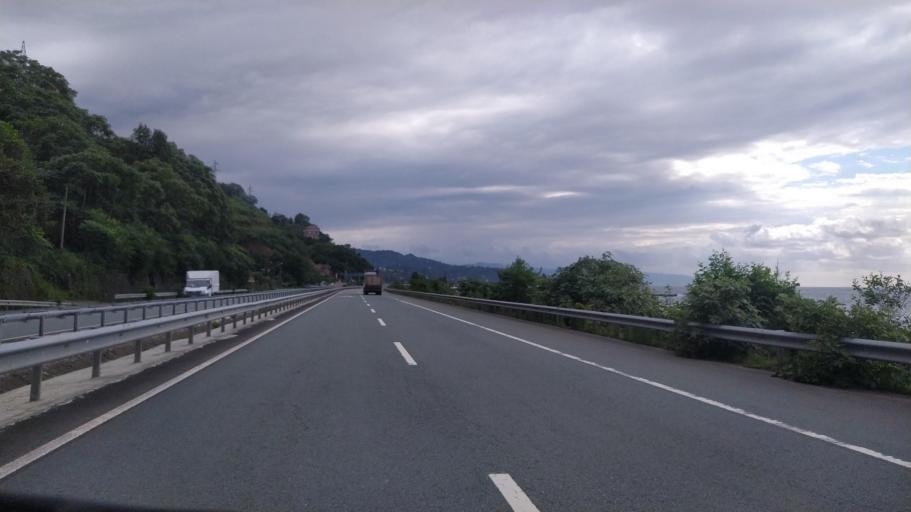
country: TR
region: Rize
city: Findikli
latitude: 41.2331
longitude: 41.0847
